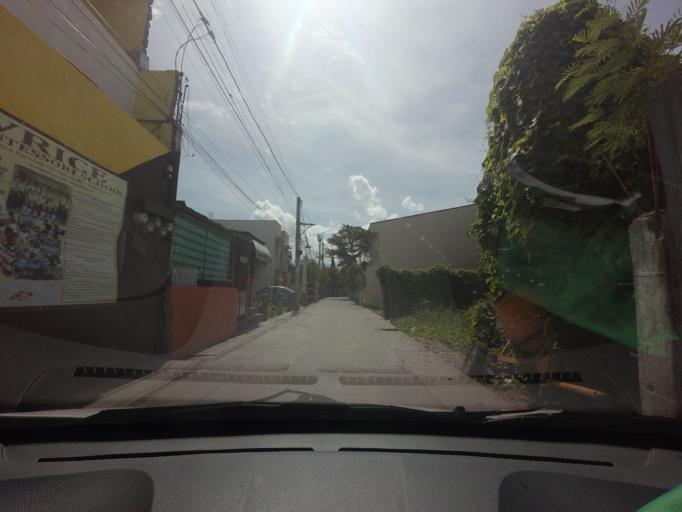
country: PH
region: Calabarzon
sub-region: Province of Rizal
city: Pateros
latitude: 14.5328
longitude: 121.0759
